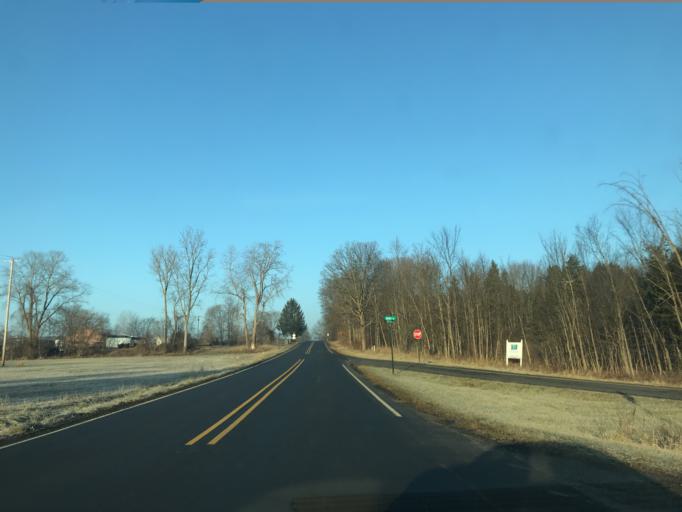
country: US
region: Michigan
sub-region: Ingham County
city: Leslie
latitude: 42.4361
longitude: -84.5406
